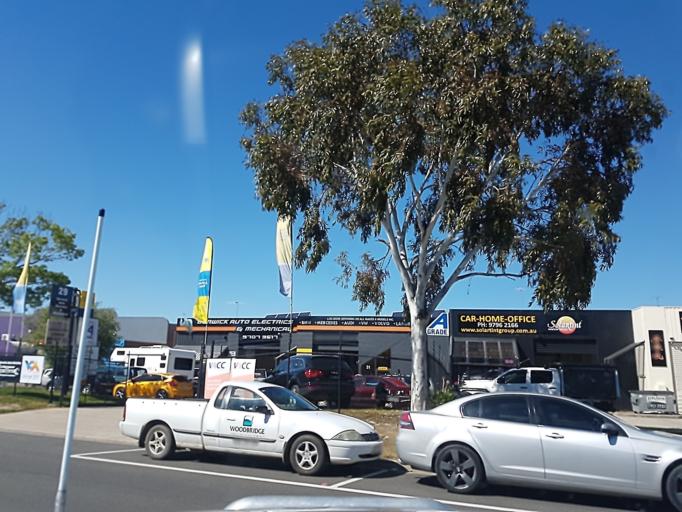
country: AU
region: Victoria
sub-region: Casey
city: Berwick
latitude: -38.0362
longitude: 145.3391
